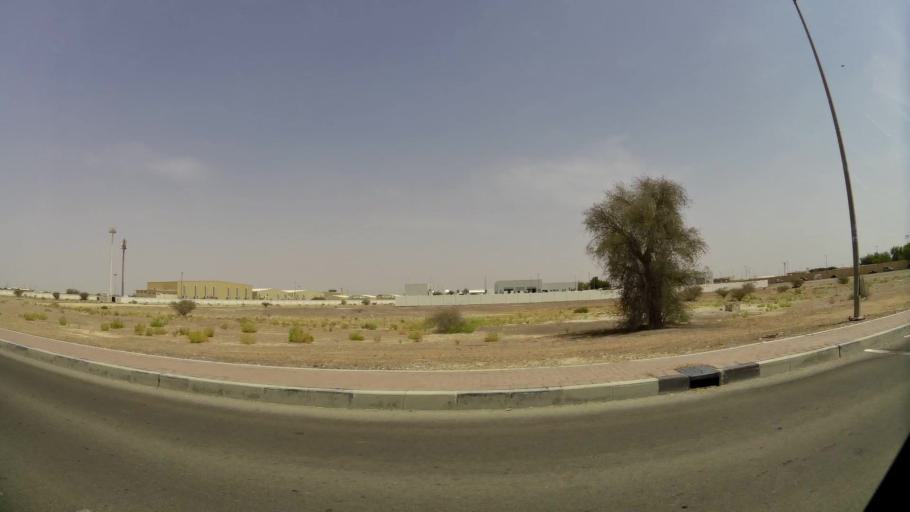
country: AE
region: Abu Dhabi
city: Al Ain
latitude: 24.1874
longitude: 55.7213
